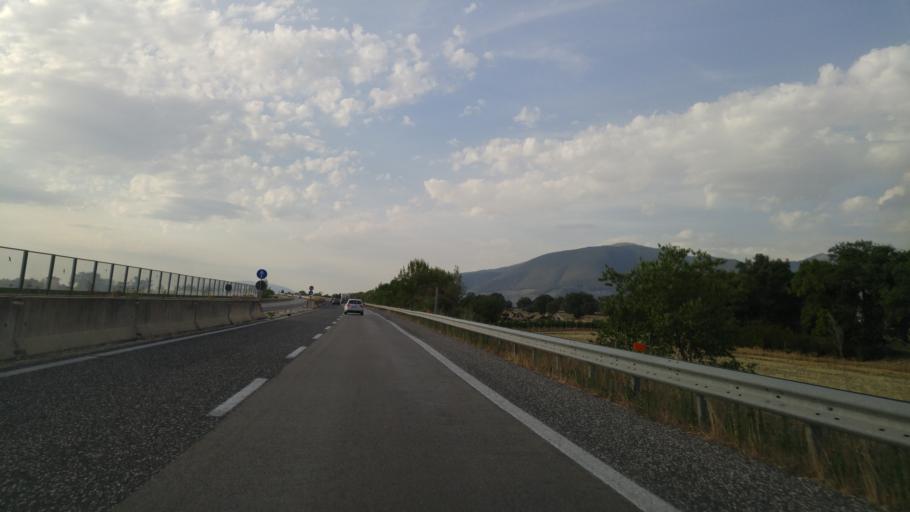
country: IT
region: Umbria
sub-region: Provincia di Perugia
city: San Giacomo
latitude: 42.7853
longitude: 12.7668
